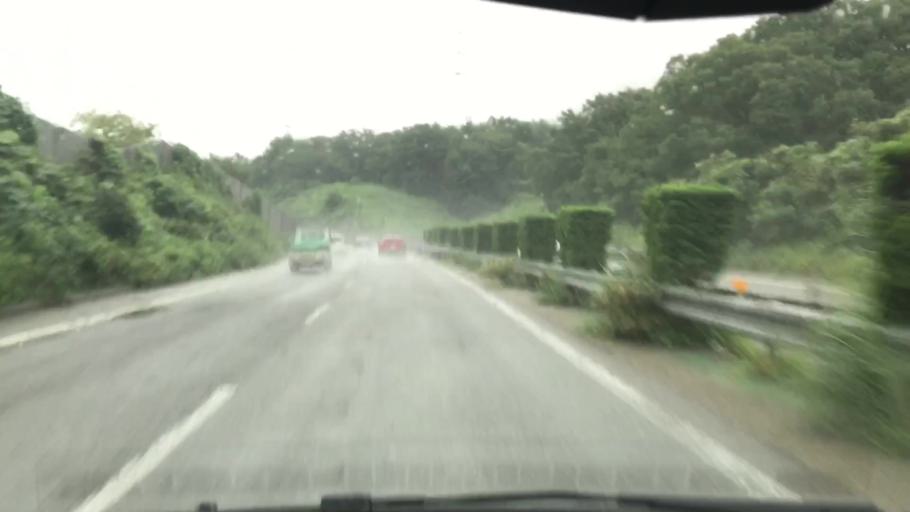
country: JP
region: Hyogo
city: Kobe
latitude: 34.7635
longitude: 135.1910
